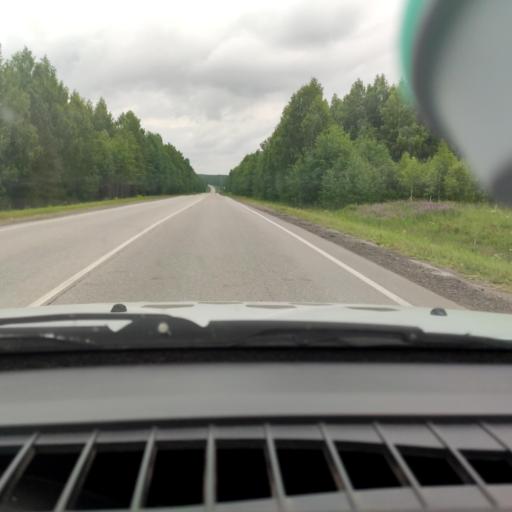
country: RU
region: Perm
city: Kungur
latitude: 57.4544
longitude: 57.0282
